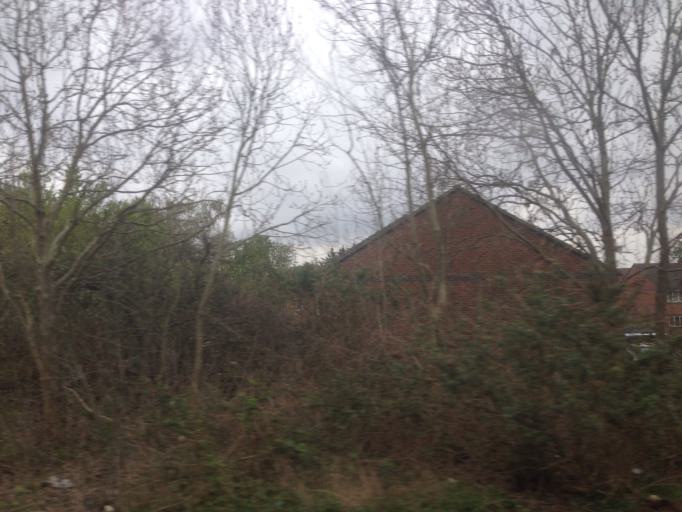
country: GB
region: England
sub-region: Greater London
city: Mitcham
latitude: 51.4158
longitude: -0.1454
